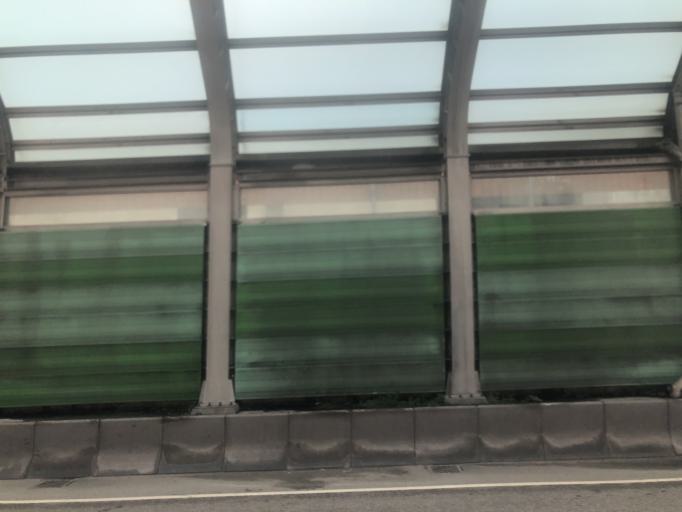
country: HK
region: Tuen Mun
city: Tuen Mun
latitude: 22.3915
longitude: 113.9776
